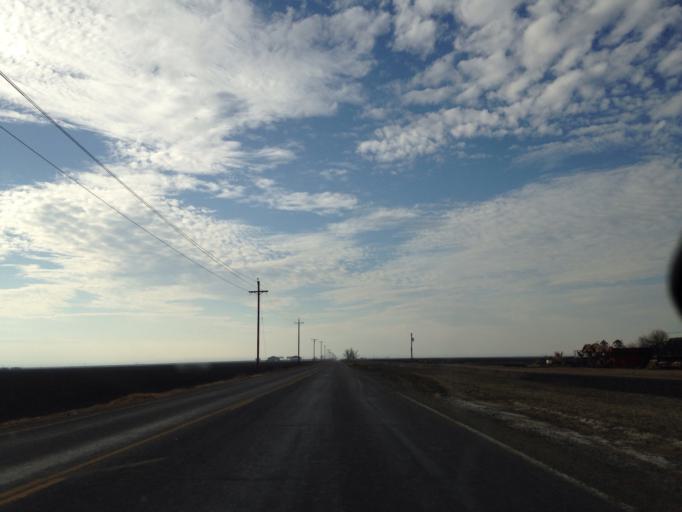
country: US
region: California
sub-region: Kern County
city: Buttonwillow
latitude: 35.4421
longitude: -119.5184
